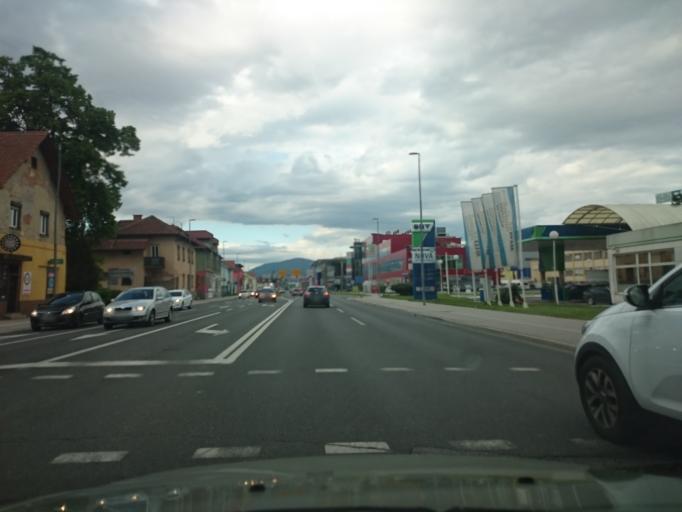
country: SI
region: Celje
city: Celje
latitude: 46.2391
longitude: 15.2740
